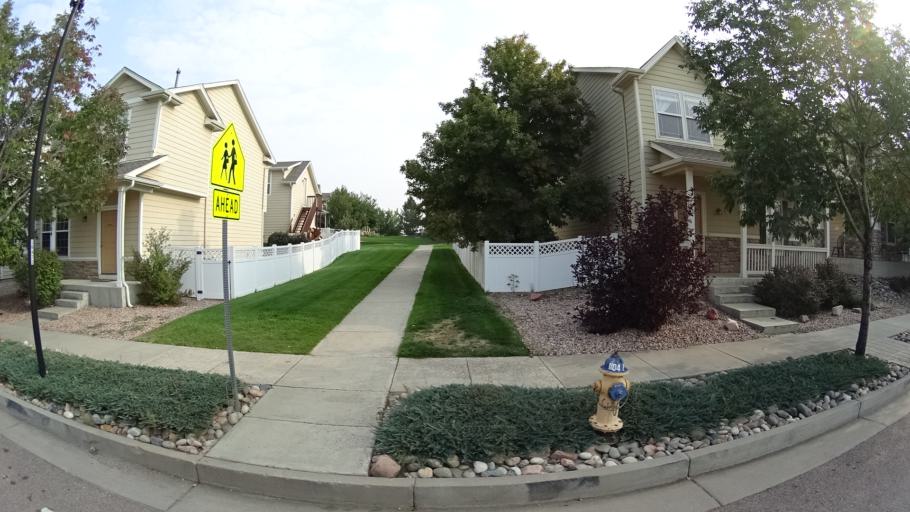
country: US
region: Colorado
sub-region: El Paso County
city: Stratmoor
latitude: 38.8064
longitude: -104.7840
